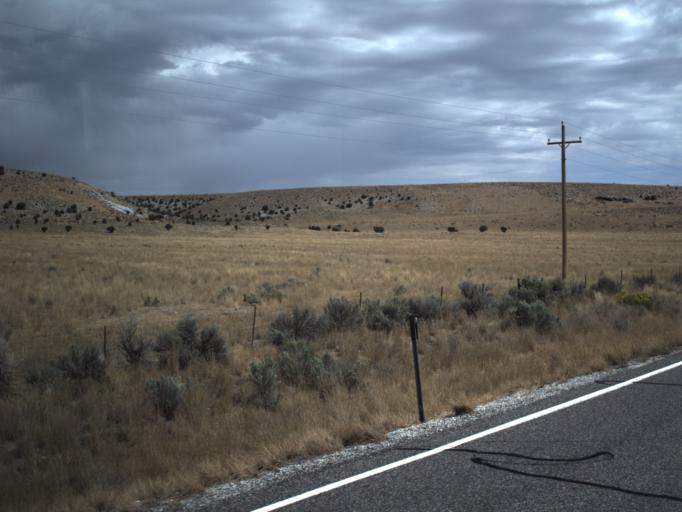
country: US
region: Idaho
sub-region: Cassia County
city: Burley
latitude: 41.8159
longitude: -113.2311
